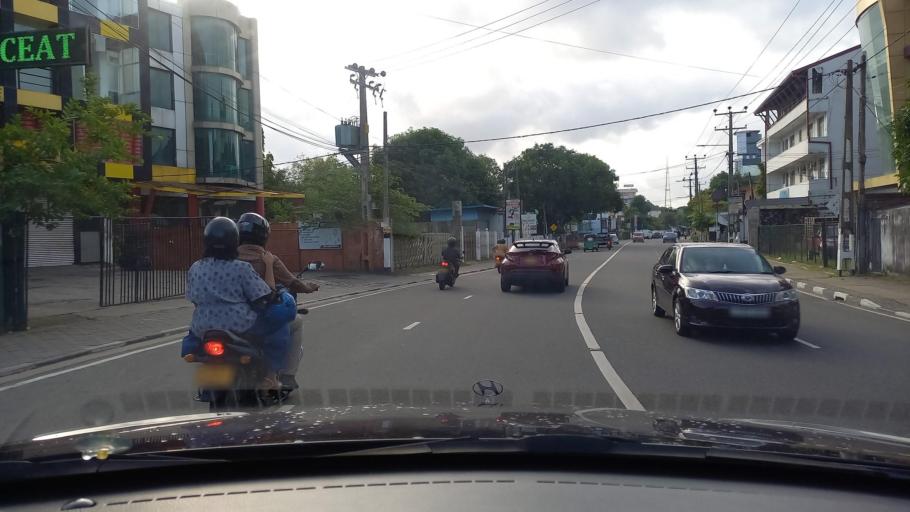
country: LK
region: Western
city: Sri Jayewardenepura Kotte
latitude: 6.8759
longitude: 79.8932
